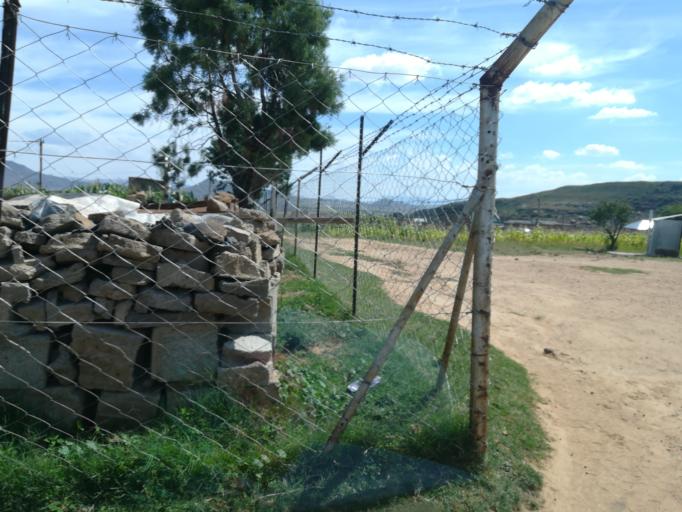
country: LS
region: Mohale's Hoek District
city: Mohale's Hoek
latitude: -30.1021
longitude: 27.4693
